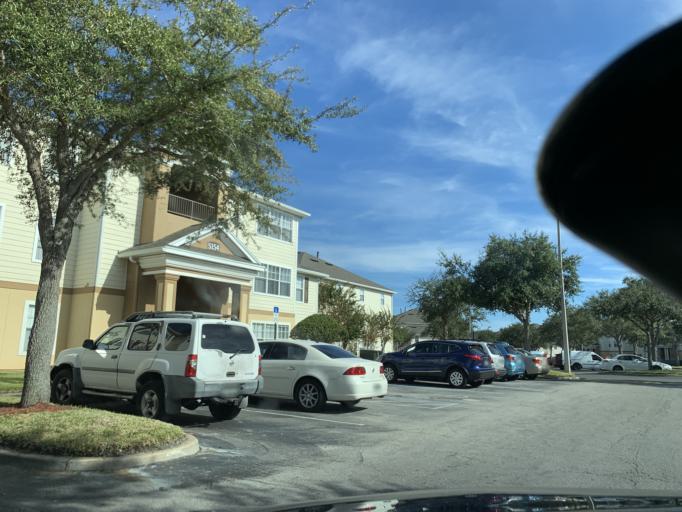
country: US
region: Florida
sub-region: Orange County
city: Oak Ridge
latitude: 28.4773
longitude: -81.4405
